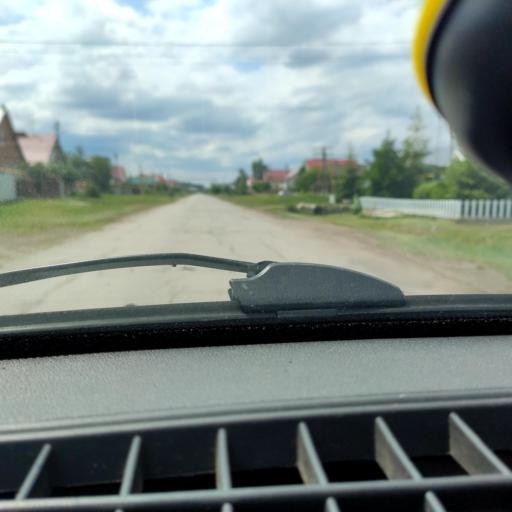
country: RU
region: Samara
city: Povolzhskiy
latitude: 53.6405
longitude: 49.6851
